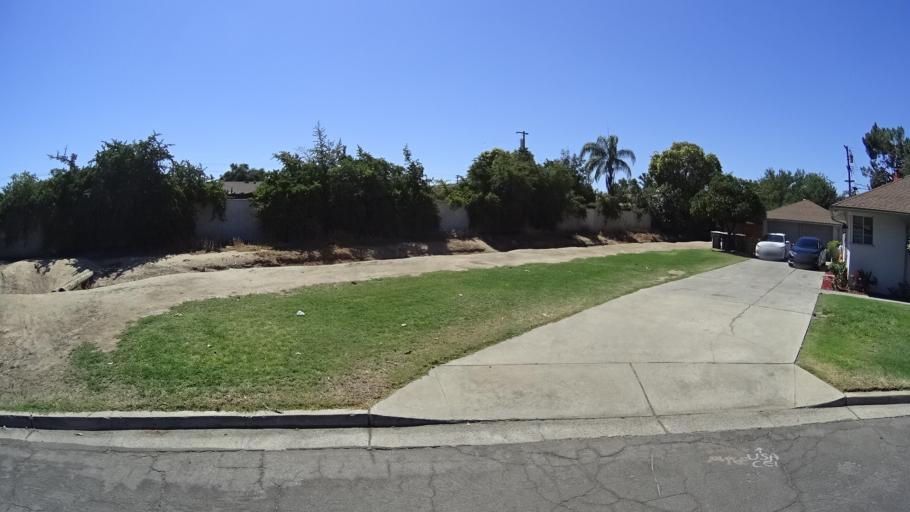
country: US
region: California
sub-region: Fresno County
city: Fresno
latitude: 36.7857
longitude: -119.8191
